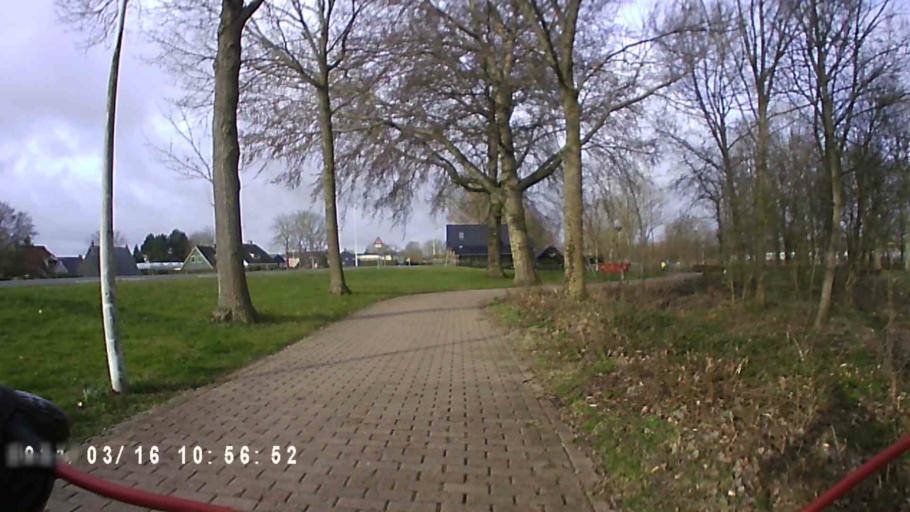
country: NL
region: Friesland
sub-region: Gemeente Dongeradeel
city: Dokkum
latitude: 53.3258
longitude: 6.0104
